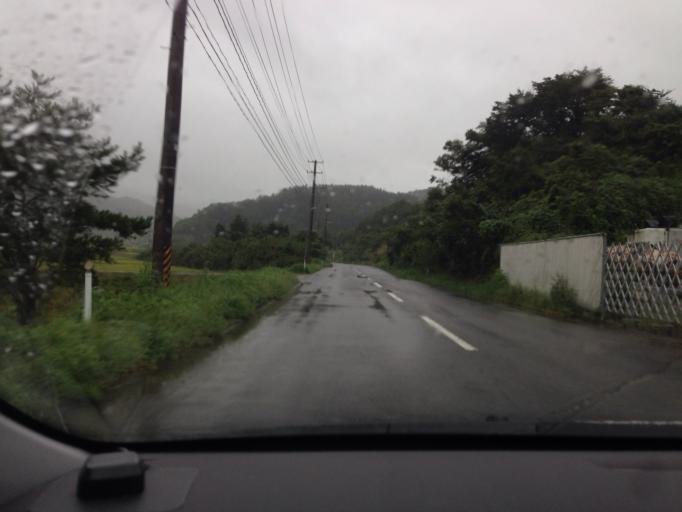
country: JP
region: Fukushima
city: Koriyama
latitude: 37.4249
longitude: 140.2729
